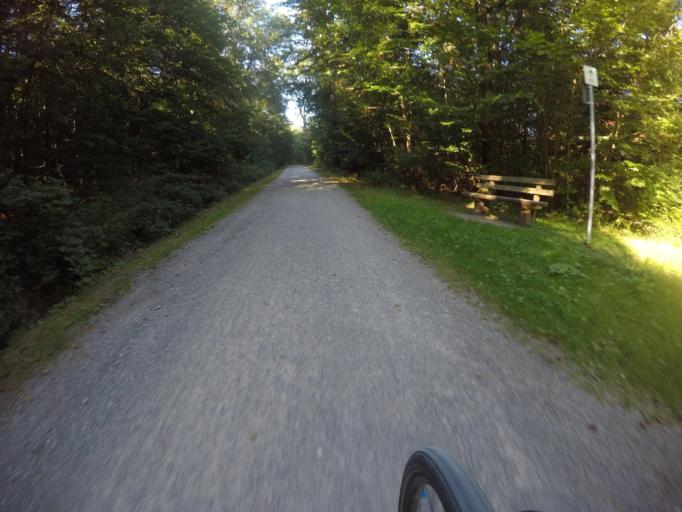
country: DE
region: Baden-Wuerttemberg
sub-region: Regierungsbezirk Stuttgart
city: Gerlingen
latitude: 48.7789
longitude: 9.1010
